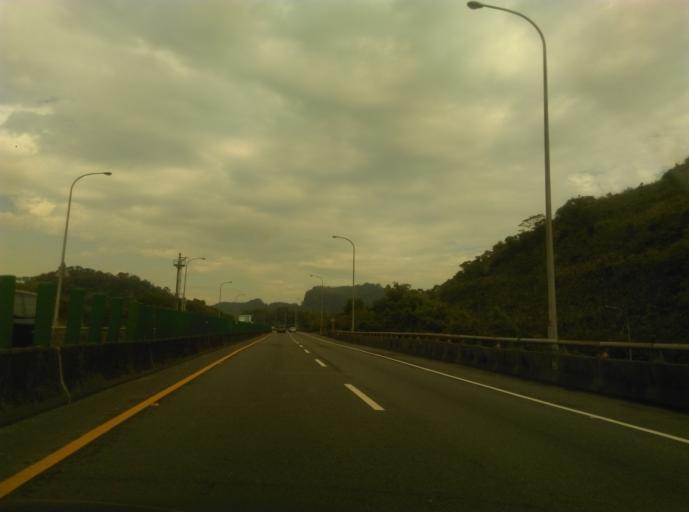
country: TW
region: Taiwan
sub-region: Keelung
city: Keelung
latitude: 25.1147
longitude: 121.6928
